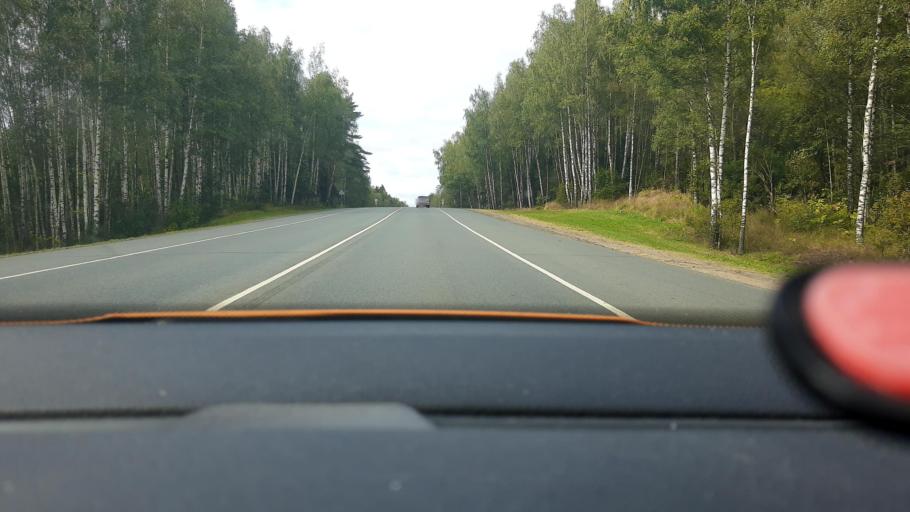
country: RU
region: Moskovskaya
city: Lesnoy
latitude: 56.0805
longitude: 38.0168
